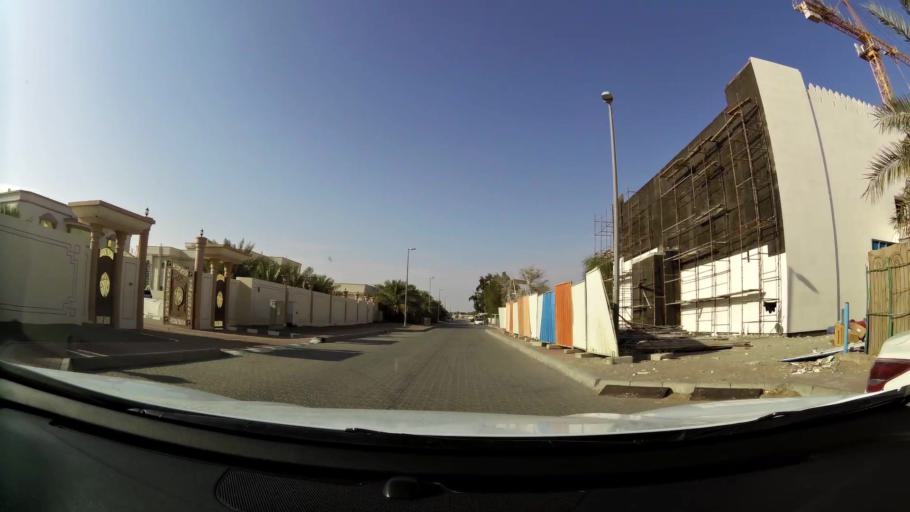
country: AE
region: Abu Dhabi
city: Al Ain
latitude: 24.0359
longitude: 55.8432
